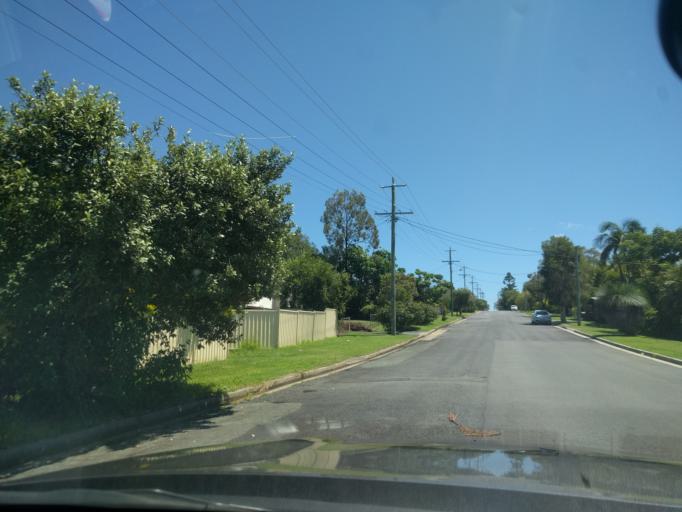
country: AU
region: Queensland
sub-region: Logan
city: Cedar Vale
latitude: -27.9922
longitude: 153.0084
